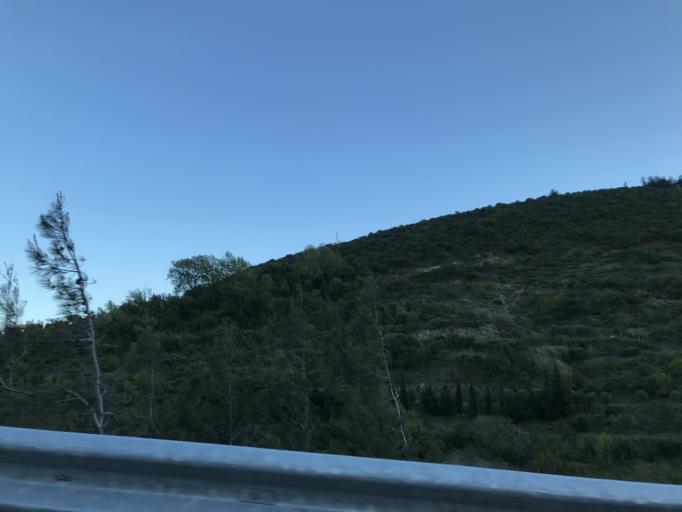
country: TR
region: Hatay
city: Buyukcat
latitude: 36.1071
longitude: 36.0498
